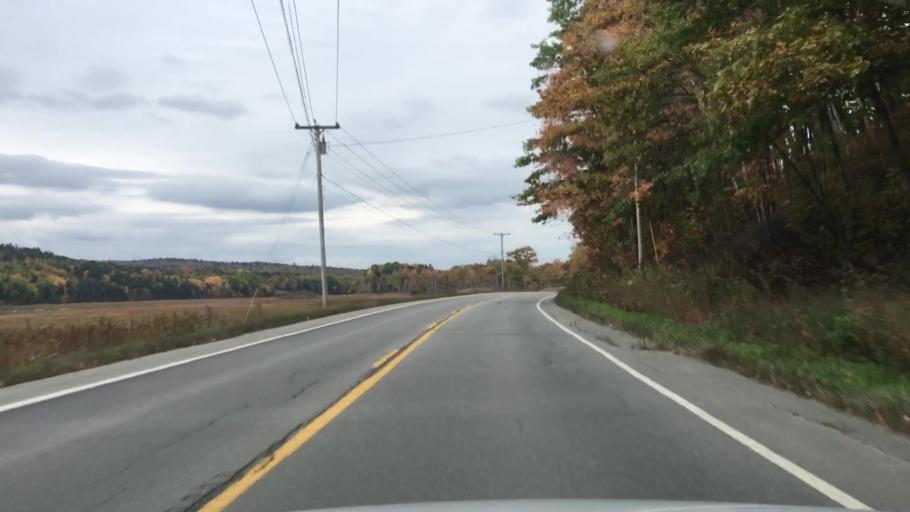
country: US
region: Maine
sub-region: Waldo County
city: Frankfort
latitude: 44.5859
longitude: -68.8638
